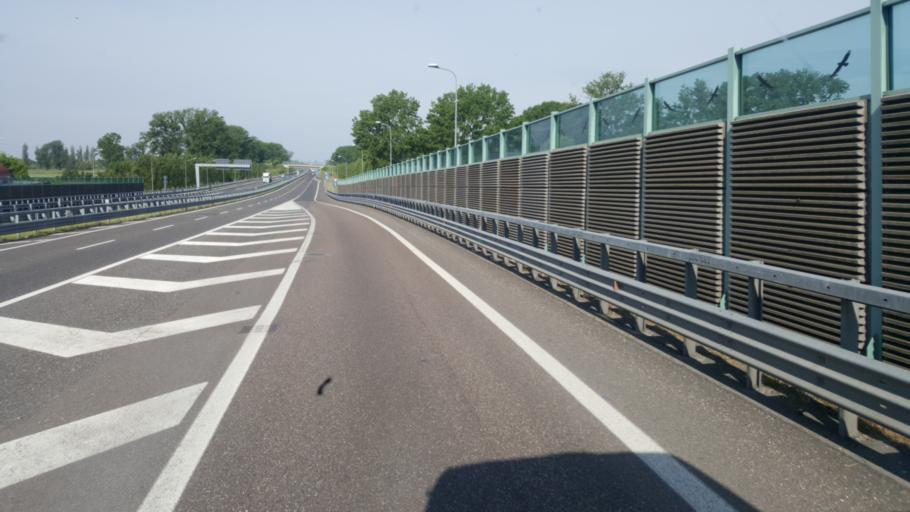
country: IT
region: Lombardy
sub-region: Citta metropolitana di Milano
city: Vignate
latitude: 45.4842
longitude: 9.3767
